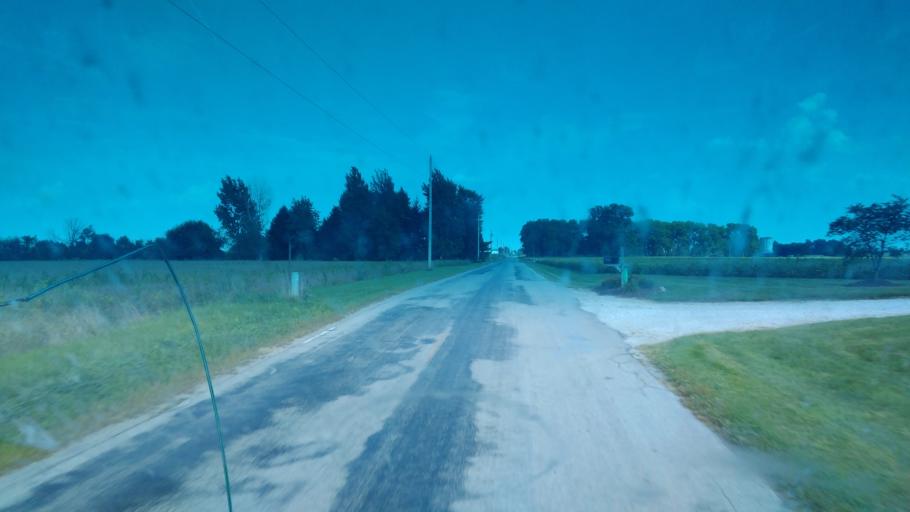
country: US
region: Ohio
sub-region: Wyandot County
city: Carey
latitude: 40.9050
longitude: -83.4650
